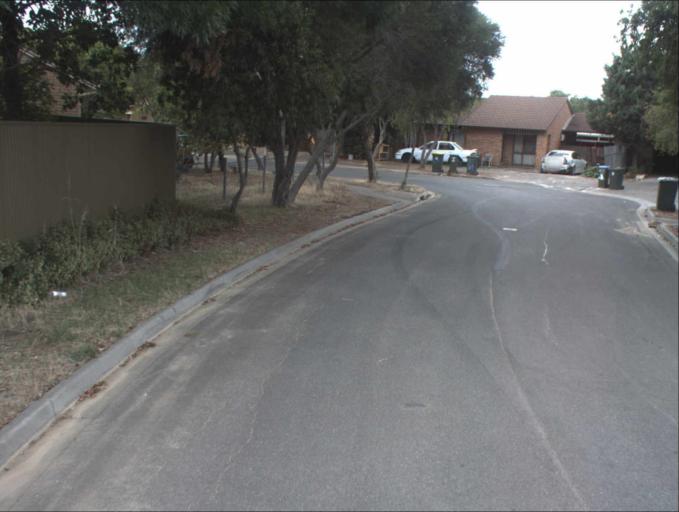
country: AU
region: South Australia
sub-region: Port Adelaide Enfield
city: Gilles Plains
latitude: -34.8515
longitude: 138.6557
